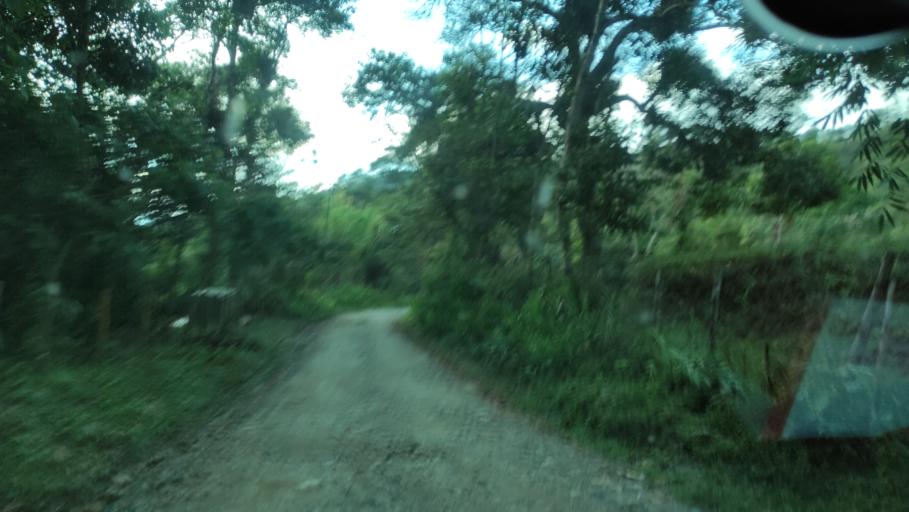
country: CO
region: Valle del Cauca
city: Buga
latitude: 3.8817
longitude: -76.1801
